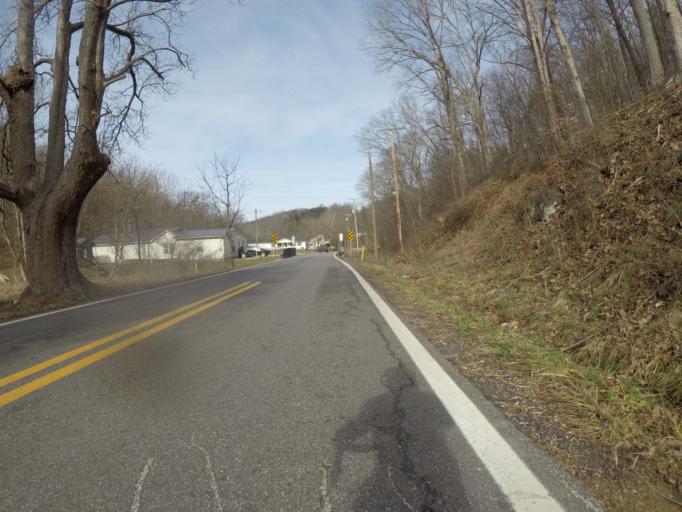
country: US
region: West Virginia
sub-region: Cabell County
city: Pea Ridge
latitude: 38.3616
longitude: -82.3723
